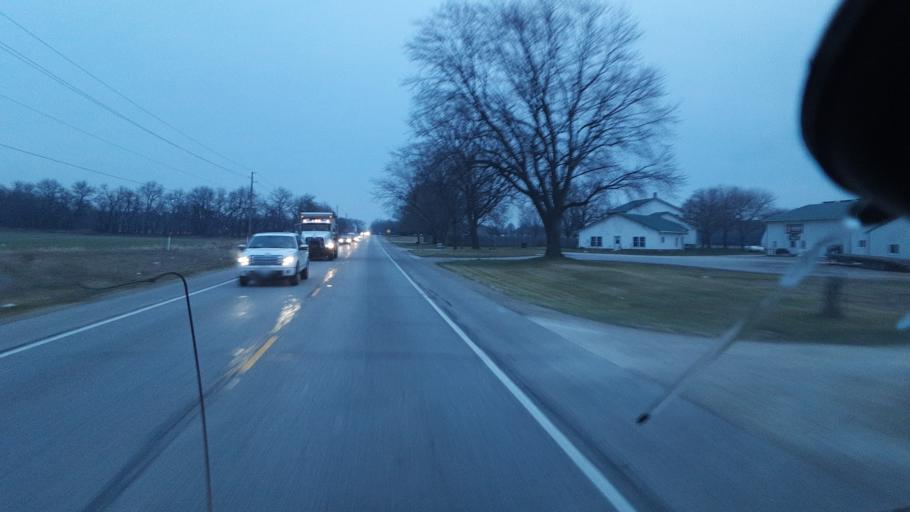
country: US
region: Indiana
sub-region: Elkhart County
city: Middlebury
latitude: 41.6677
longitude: -85.7643
